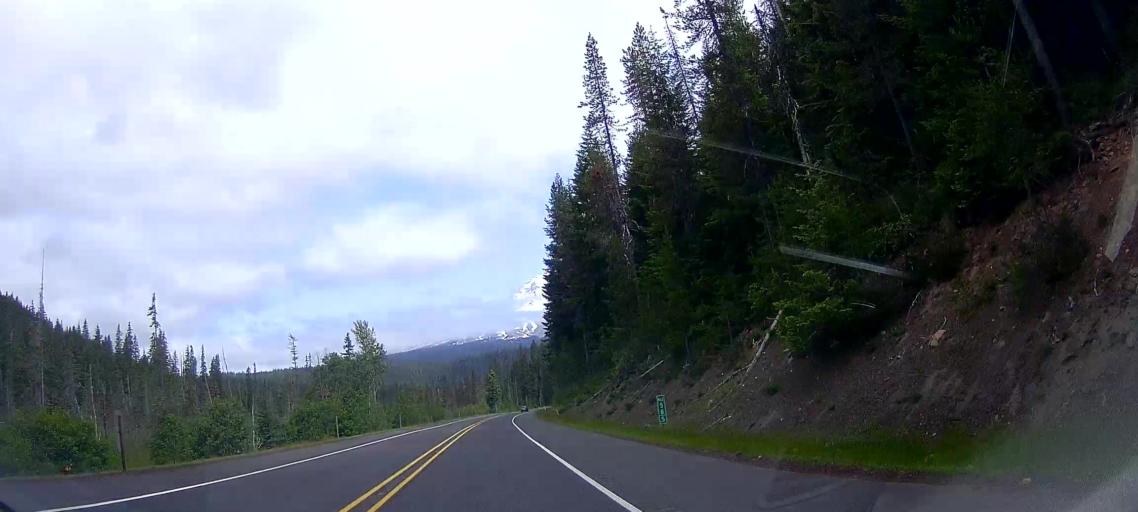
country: US
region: Oregon
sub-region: Clackamas County
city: Mount Hood Village
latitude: 45.2708
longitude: -121.7182
